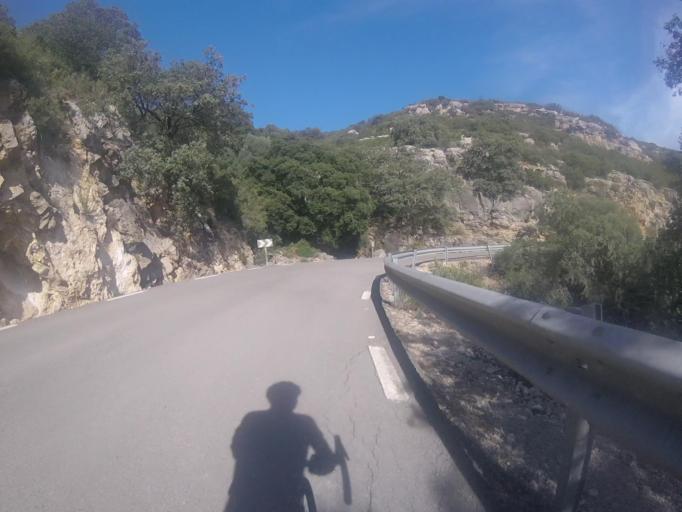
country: ES
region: Valencia
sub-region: Provincia de Castello
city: Sarratella
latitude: 40.2797
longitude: 0.0353
